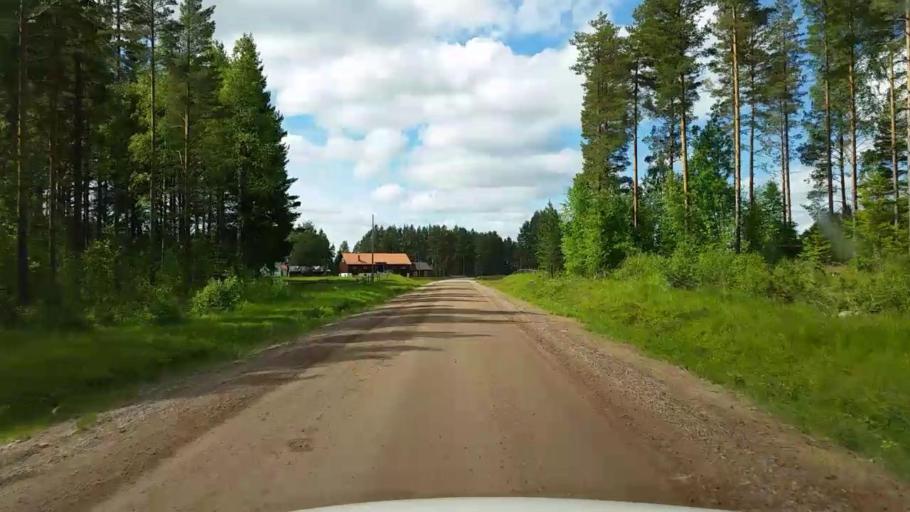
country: SE
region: Gaevleborg
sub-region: Ovanakers Kommun
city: Alfta
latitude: 61.4779
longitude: 16.0004
